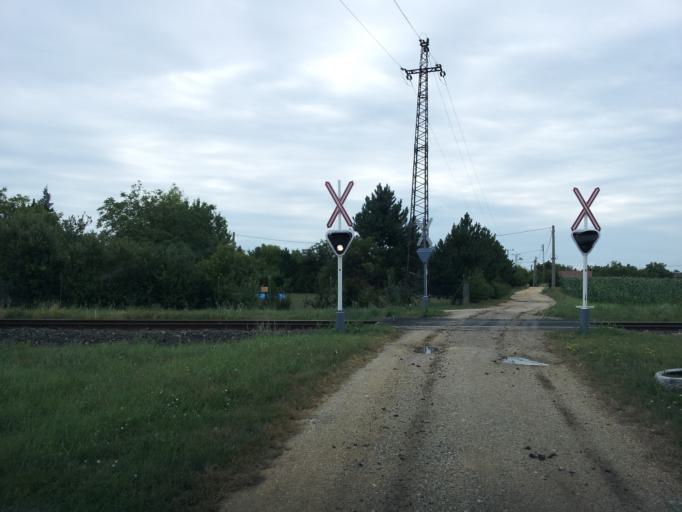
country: HU
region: Veszprem
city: Balatonkenese
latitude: 47.0214
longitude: 18.1760
